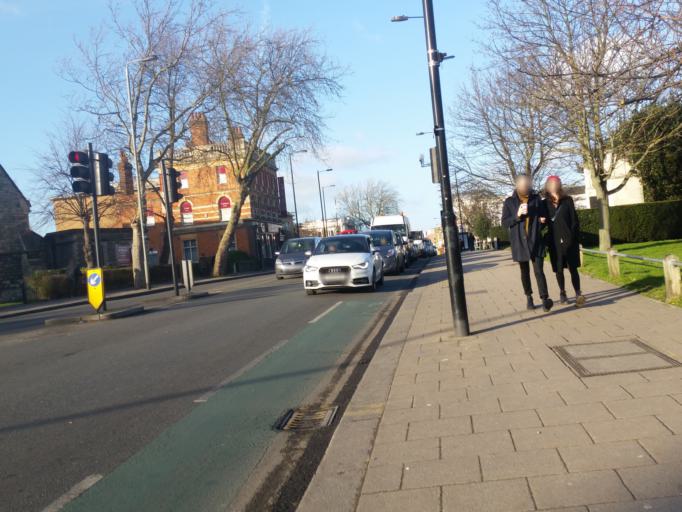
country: GB
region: England
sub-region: Greater London
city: Wood Green
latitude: 51.5991
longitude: -0.1110
